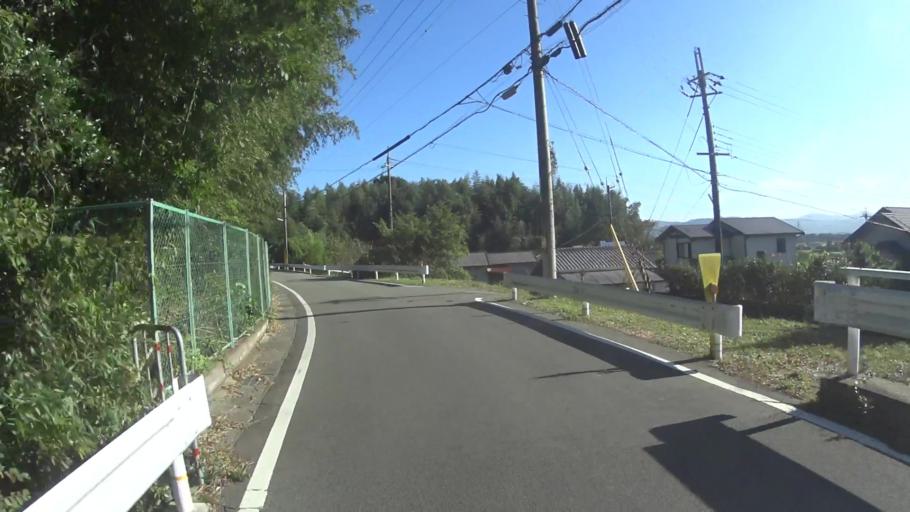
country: JP
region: Kyoto
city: Kameoka
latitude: 35.0633
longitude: 135.5737
